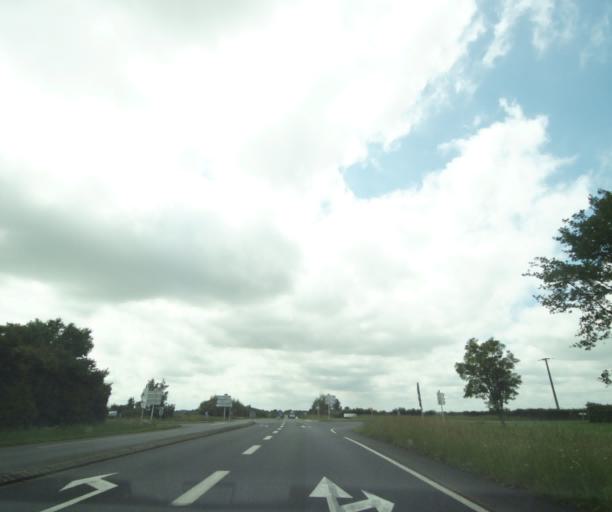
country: FR
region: Poitou-Charentes
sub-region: Departement des Deux-Sevres
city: Viennay
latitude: 46.7750
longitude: -0.2191
